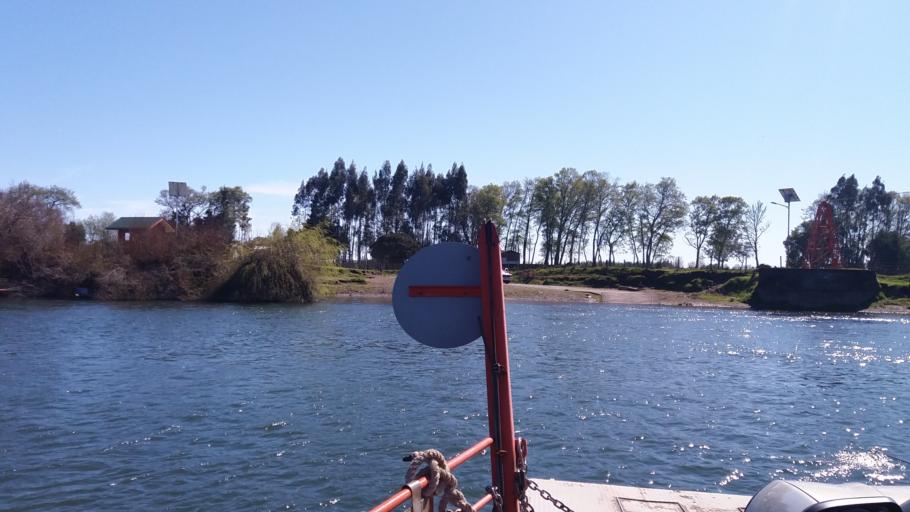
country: CL
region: Araucania
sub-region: Provincia de Cautin
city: Carahue
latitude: -39.1731
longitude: -73.1729
